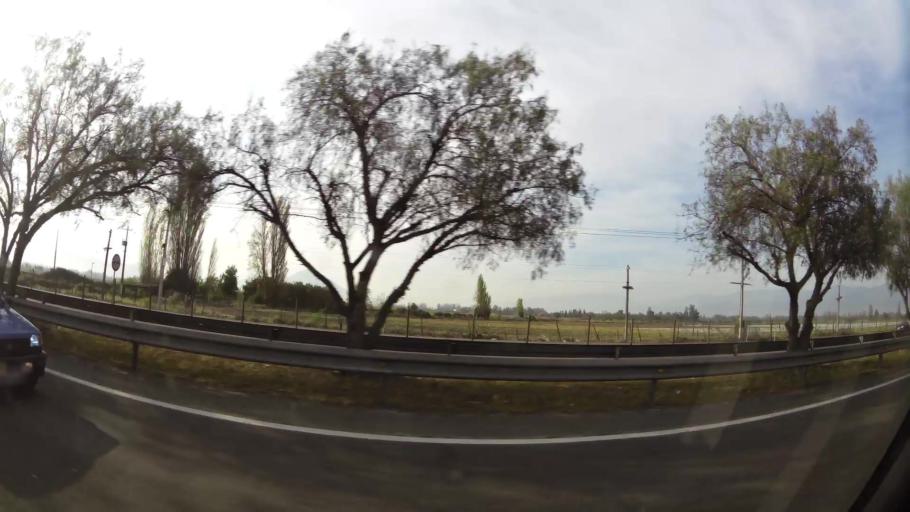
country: CL
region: Santiago Metropolitan
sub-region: Provincia de Talagante
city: Talagante
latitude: -33.6620
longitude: -70.9024
